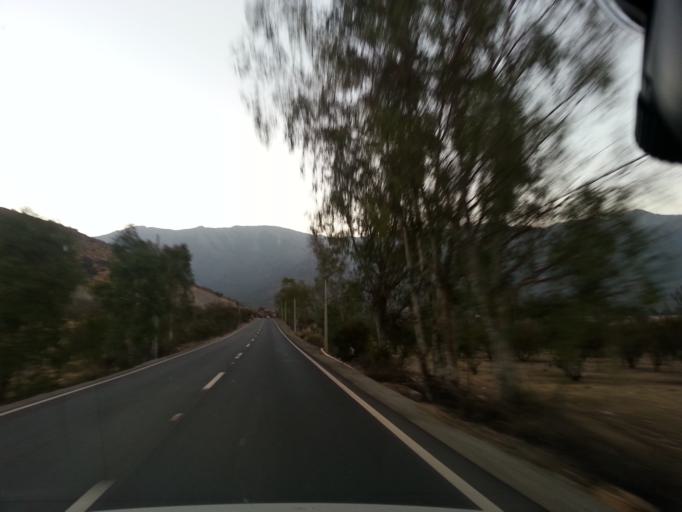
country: CL
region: Santiago Metropolitan
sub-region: Provincia de Chacabuco
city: Lampa
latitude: -33.2450
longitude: -70.9177
